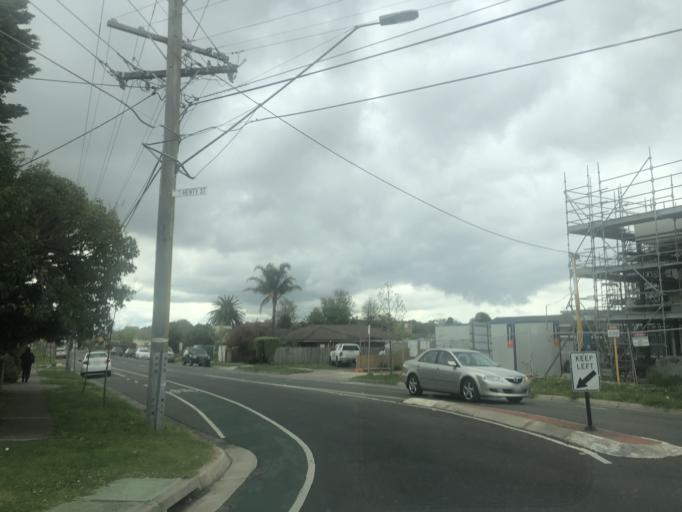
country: AU
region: Victoria
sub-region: Greater Dandenong
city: Dandenong
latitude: -37.9802
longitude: 145.2128
